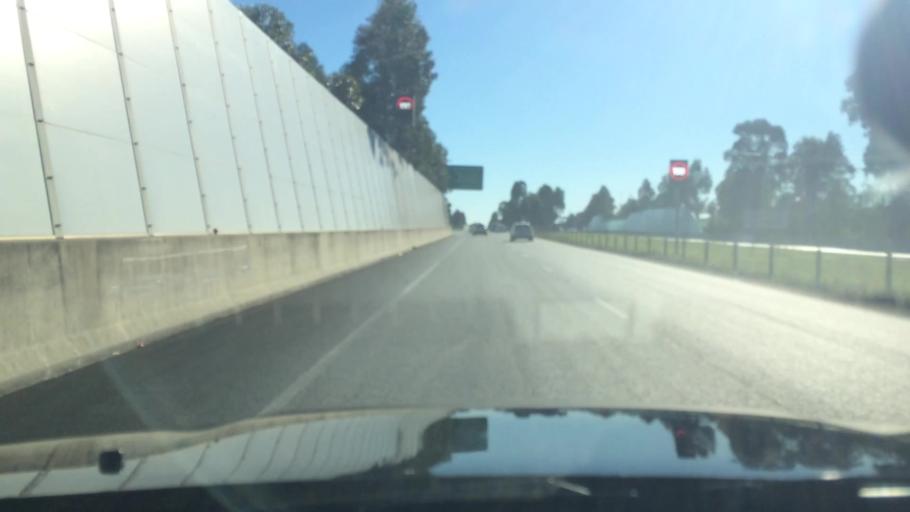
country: AU
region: New South Wales
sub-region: Blacktown
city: Glendenning
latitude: -33.7402
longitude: 150.8475
